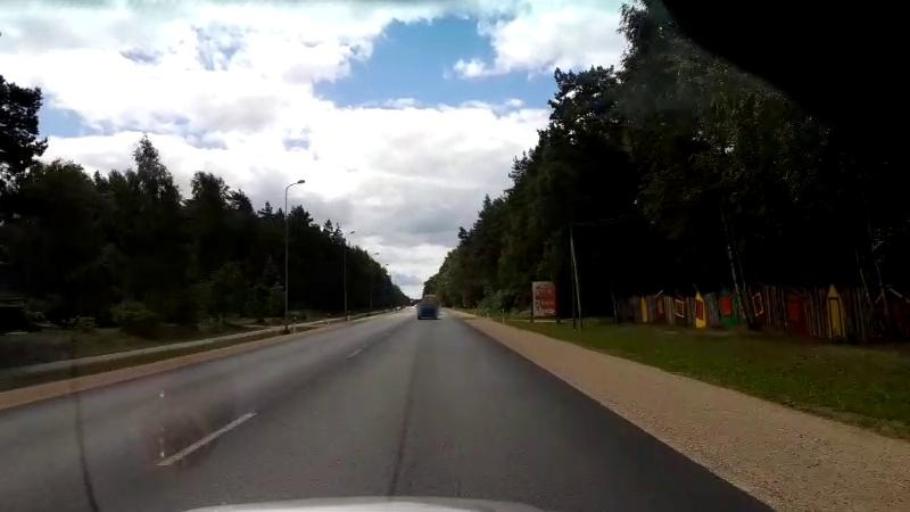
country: LV
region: Salacgrivas
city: Salacgriva
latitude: 57.7760
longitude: 24.3550
